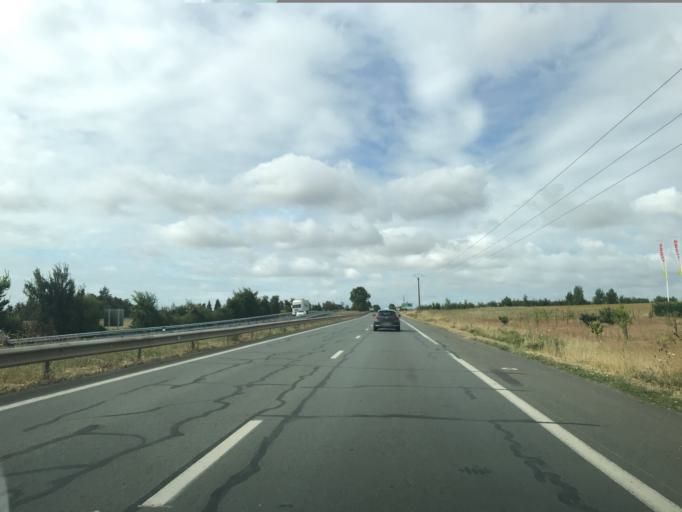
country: FR
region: Poitou-Charentes
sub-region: Departement de la Vienne
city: Vivonne
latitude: 46.4174
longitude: 0.2484
